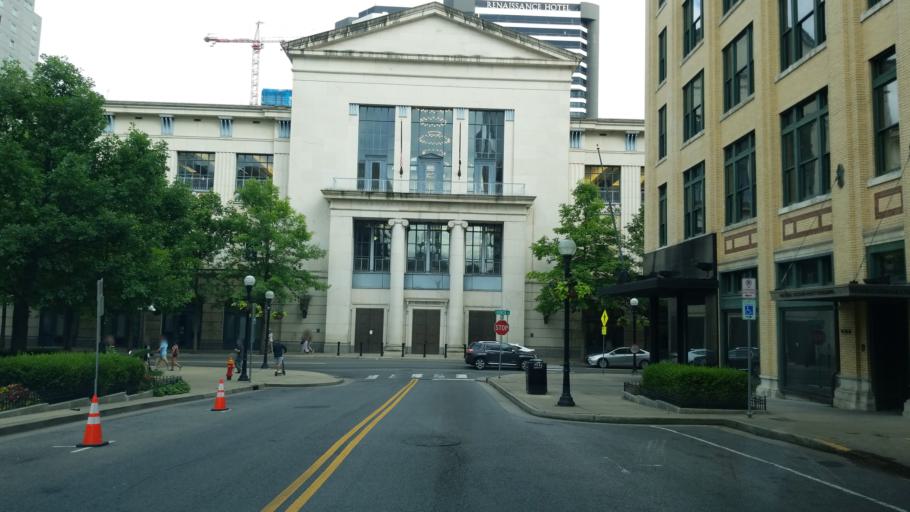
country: US
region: Tennessee
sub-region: Davidson County
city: Nashville
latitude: 36.1627
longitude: -86.7823
